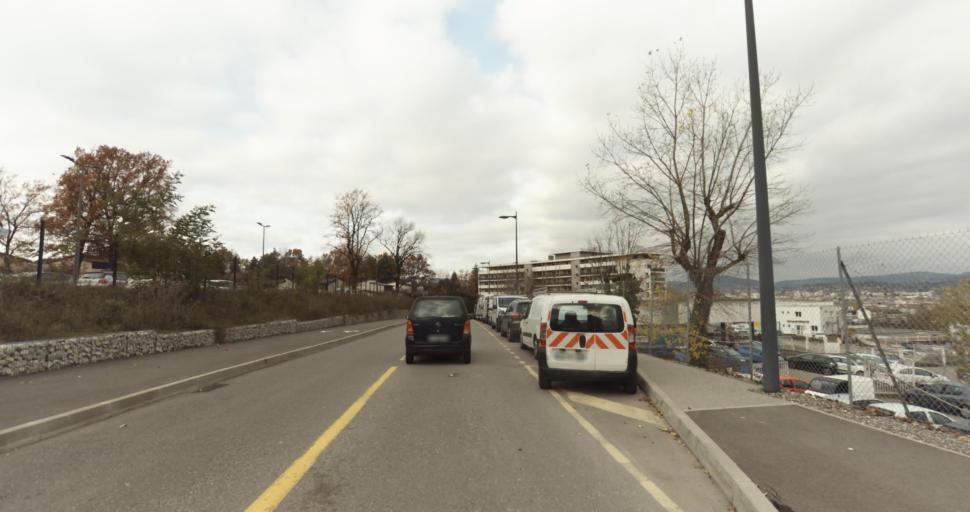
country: FR
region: Rhone-Alpes
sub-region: Departement de la Haute-Savoie
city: Annecy
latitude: 45.8925
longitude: 6.1090
